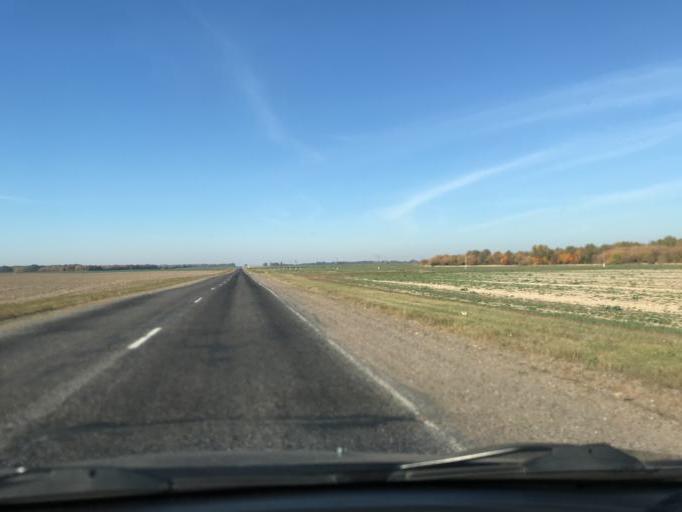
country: BY
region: Gomel
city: Brahin
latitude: 51.7898
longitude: 30.1820
